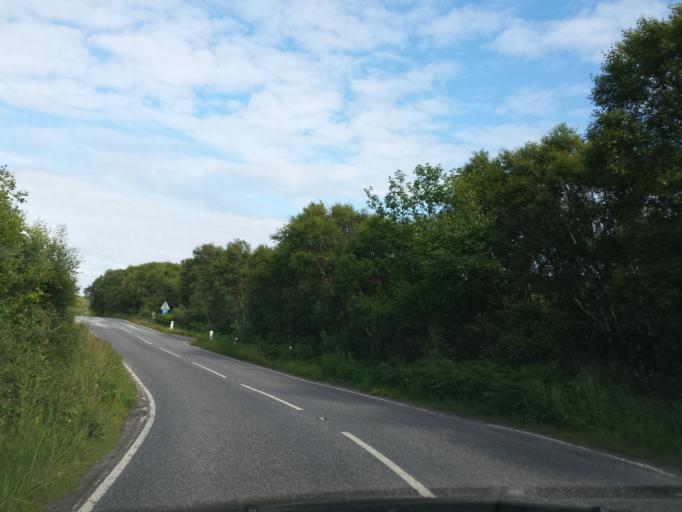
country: GB
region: Scotland
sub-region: Argyll and Bute
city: Isle Of Mull
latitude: 56.9615
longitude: -5.8266
